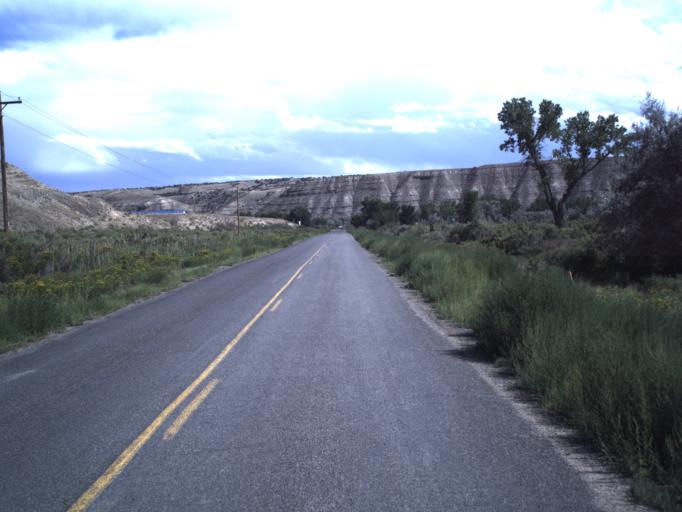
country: US
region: Utah
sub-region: Duchesne County
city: Duchesne
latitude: 40.1686
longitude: -110.4170
